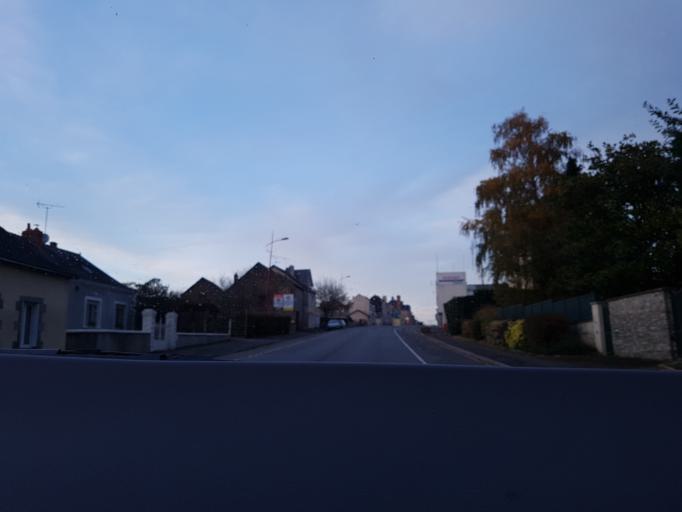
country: FR
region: Pays de la Loire
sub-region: Departement de la Mayenne
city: Cosse-le-Vivien
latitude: 47.9417
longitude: -0.9143
